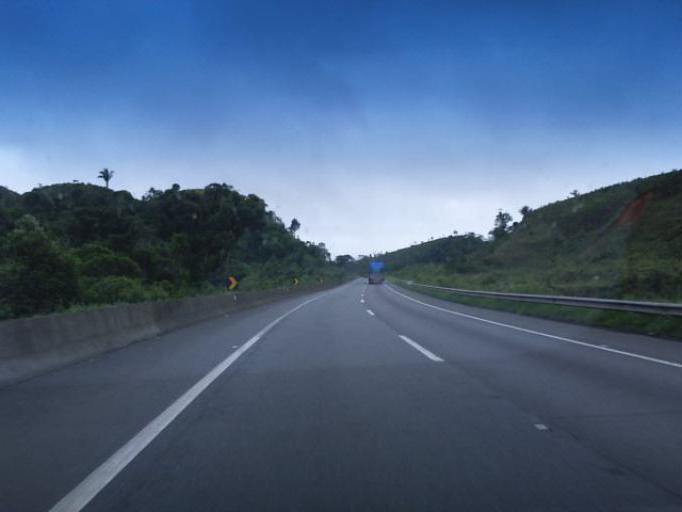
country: BR
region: Parana
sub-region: Antonina
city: Antonina
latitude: -25.0440
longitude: -48.5416
